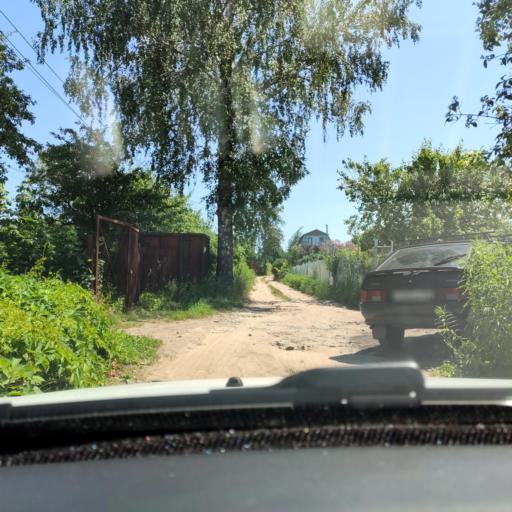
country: RU
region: Voronezj
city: Shilovo
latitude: 51.5939
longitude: 39.1438
